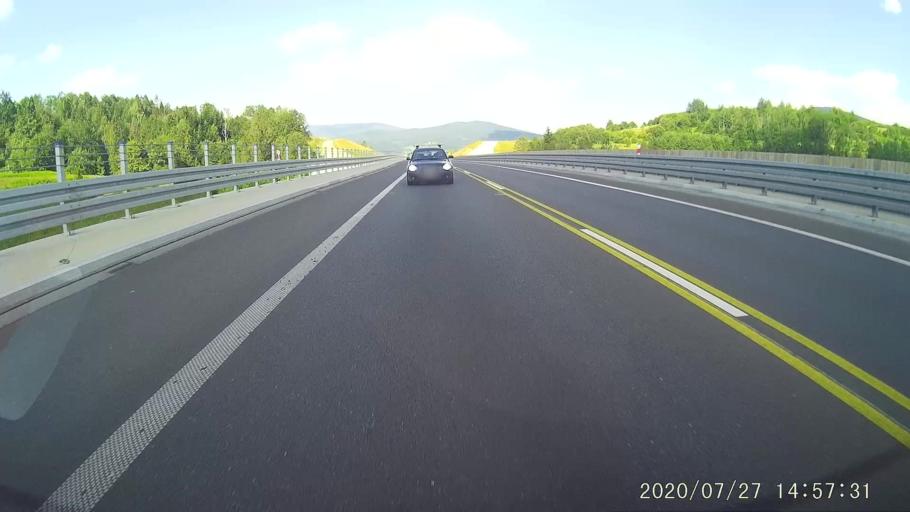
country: PL
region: Lesser Poland Voivodeship
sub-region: Powiat myslenicki
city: Lubien
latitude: 49.6975
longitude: 19.9398
